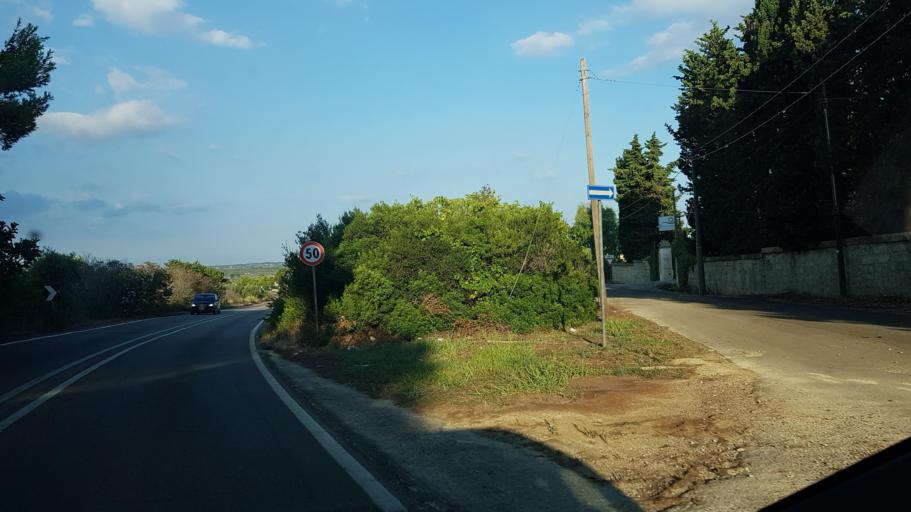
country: IT
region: Apulia
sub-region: Provincia di Lecce
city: Gemini
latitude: 39.8671
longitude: 18.2118
